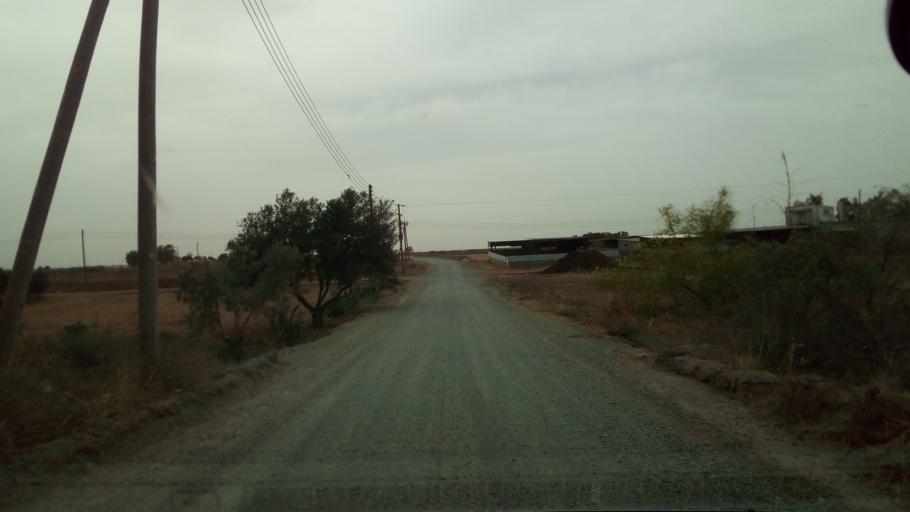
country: CY
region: Larnaka
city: Xylotymbou
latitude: 35.0185
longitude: 33.7310
